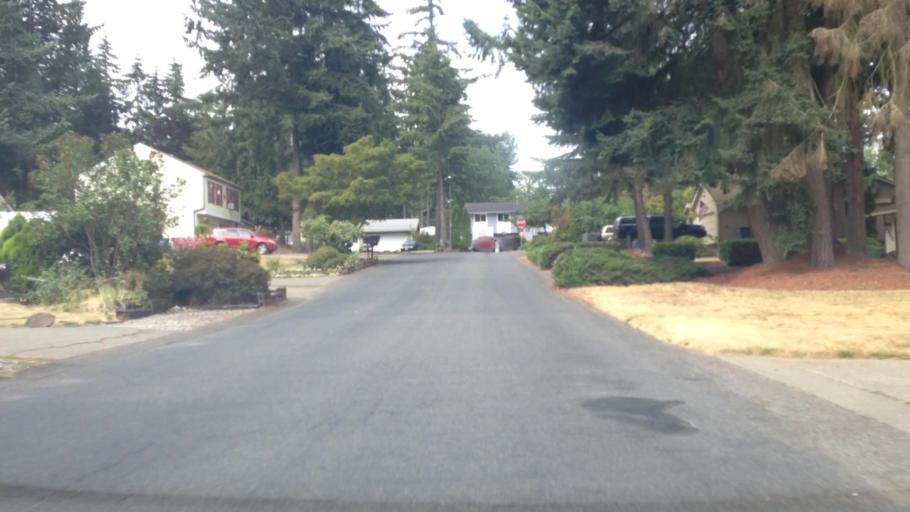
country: US
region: Washington
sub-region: Pierce County
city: South Hill
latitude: 47.1144
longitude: -122.3008
